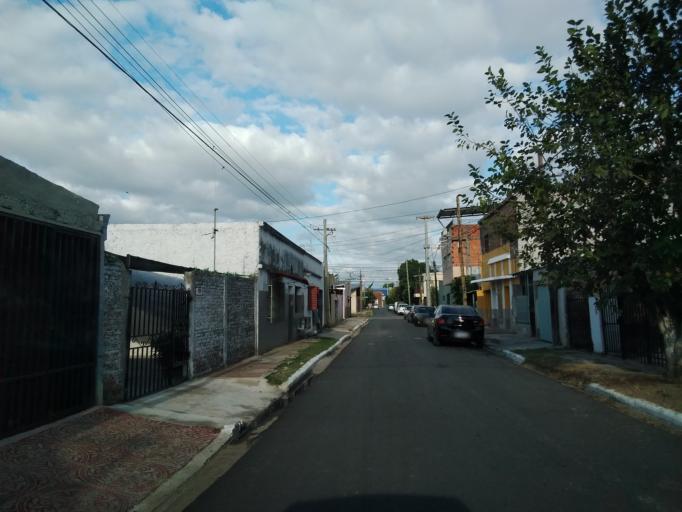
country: AR
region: Corrientes
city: Corrientes
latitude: -27.4665
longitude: -58.8149
